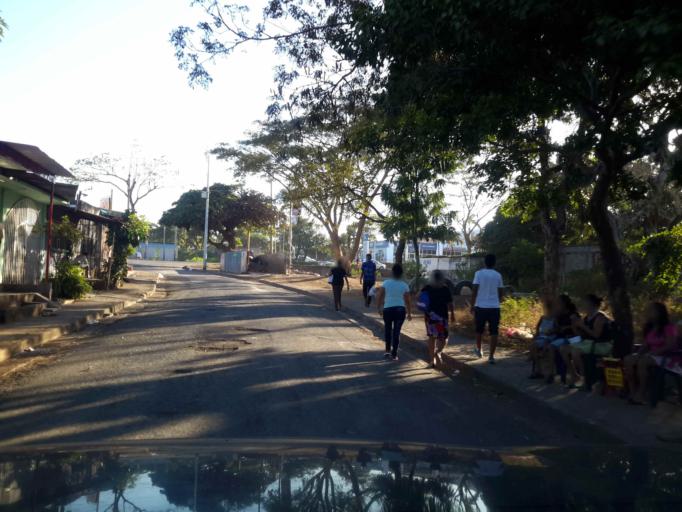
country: NI
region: Managua
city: Managua
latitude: 12.1267
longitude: -86.2887
